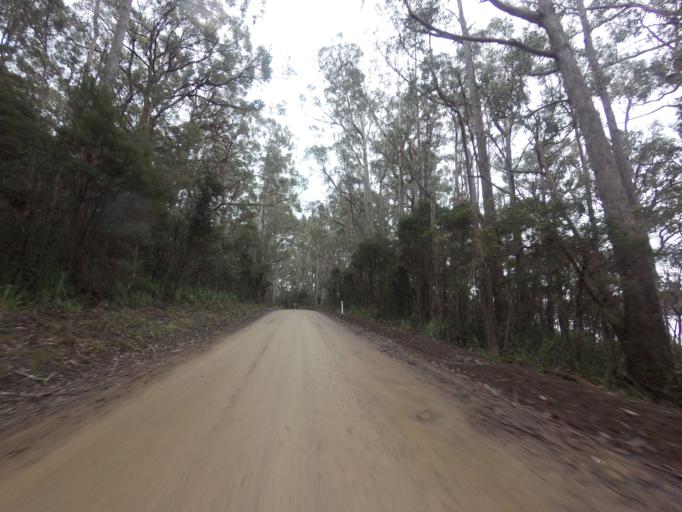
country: AU
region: Tasmania
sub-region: Huon Valley
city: Geeveston
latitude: -43.5293
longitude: 146.8956
